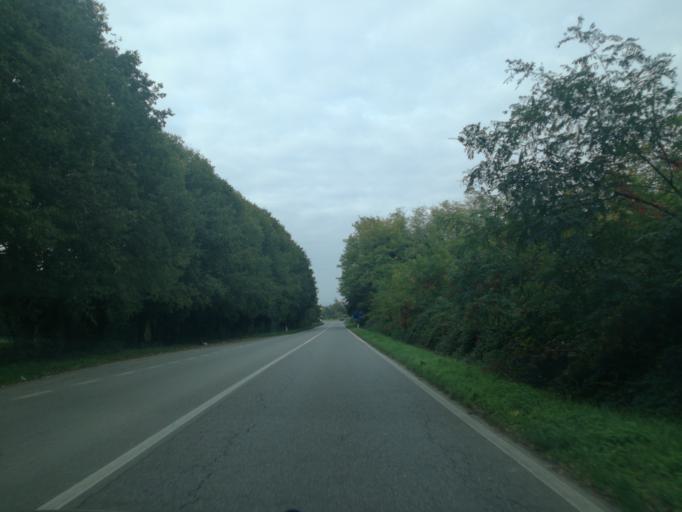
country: IT
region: Lombardy
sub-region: Provincia di Monza e Brianza
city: Aicurzio
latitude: 45.6344
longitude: 9.4130
